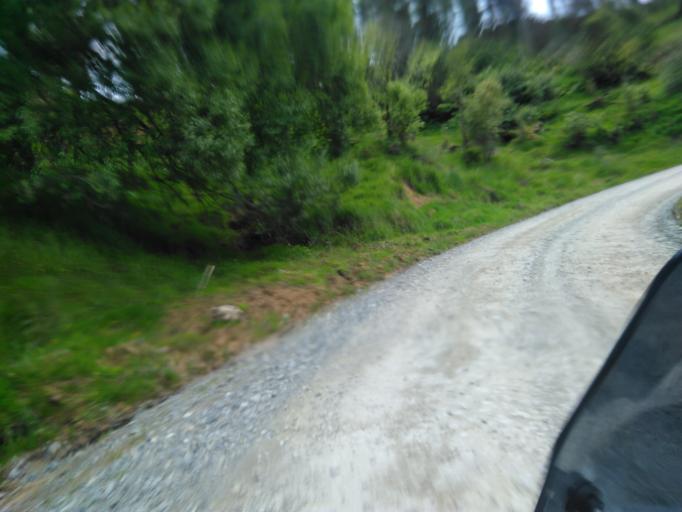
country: NZ
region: Gisborne
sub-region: Gisborne District
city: Gisborne
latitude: -38.0965
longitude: 178.1046
